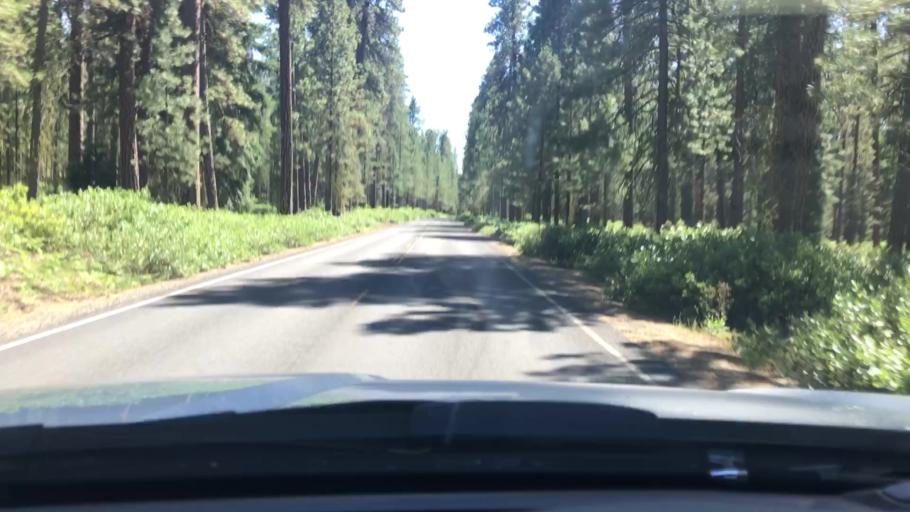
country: US
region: Oregon
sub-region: Deschutes County
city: Sisters
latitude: 44.4163
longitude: -121.6707
